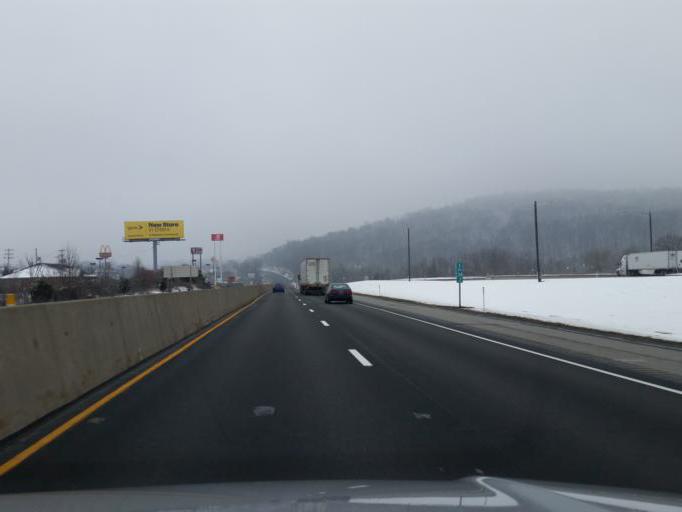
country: US
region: Pennsylvania
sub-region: York County
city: Valley Green
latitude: 40.1561
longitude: -76.8226
